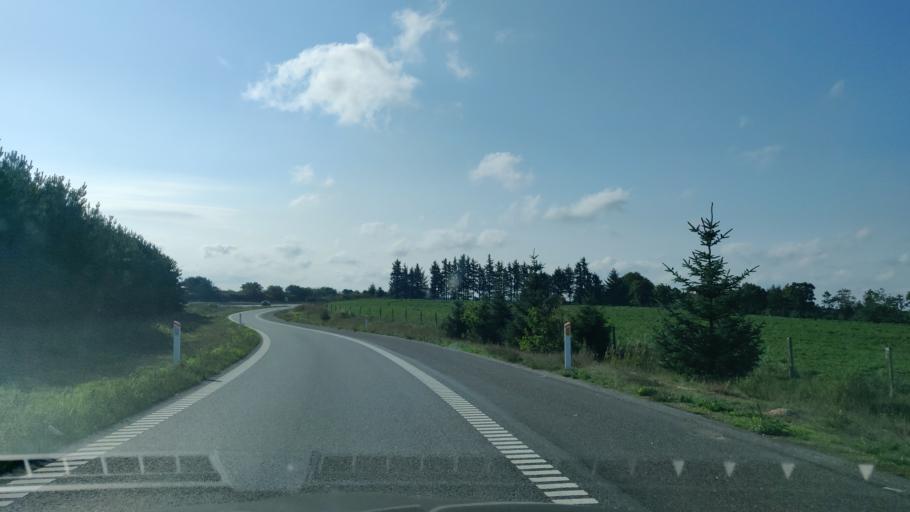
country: DK
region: North Denmark
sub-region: Hjorring Kommune
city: Vra
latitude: 57.3613
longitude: 10.0266
